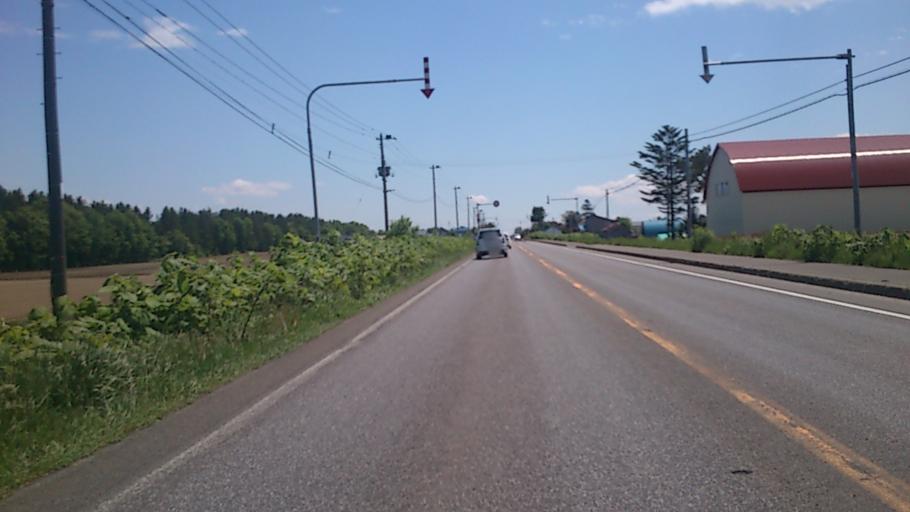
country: JP
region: Hokkaido
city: Nayoro
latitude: 44.2505
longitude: 142.3947
